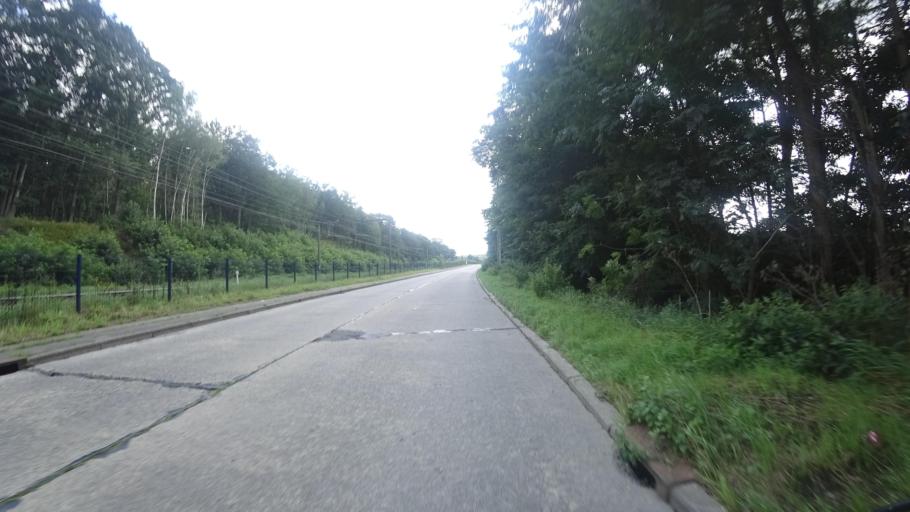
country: BE
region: Wallonia
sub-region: Province du Brabant Wallon
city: Grez-Doiceau
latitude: 50.7574
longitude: 4.6599
